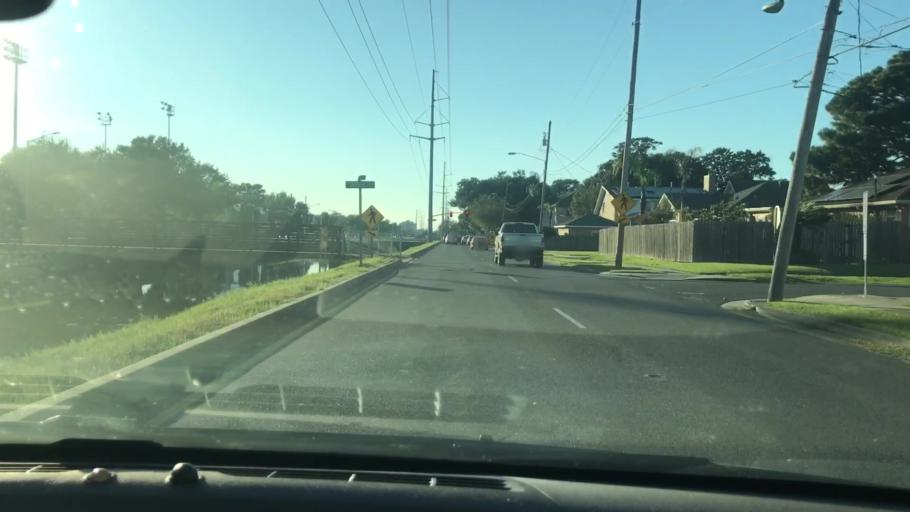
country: US
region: Louisiana
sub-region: Jefferson Parish
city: Metairie
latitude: 30.0135
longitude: -90.1303
